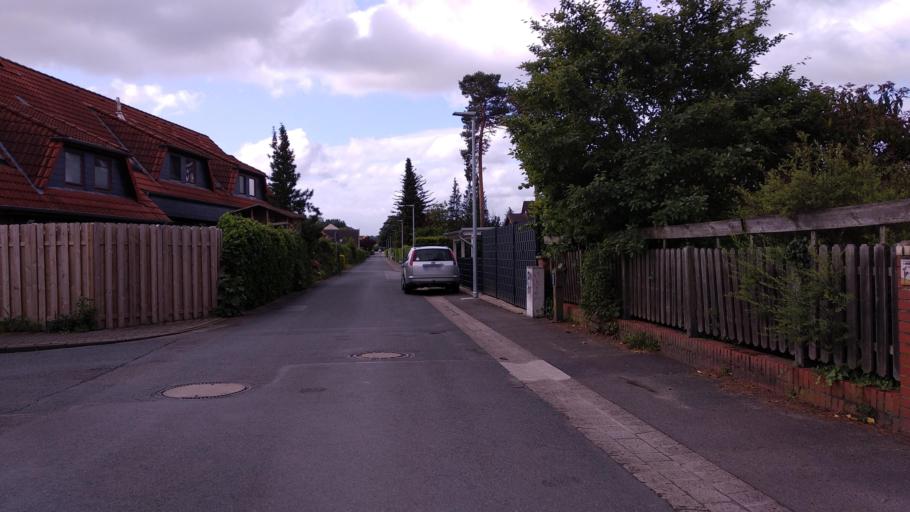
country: DE
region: Lower Saxony
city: Hagenburg
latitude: 52.4590
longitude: 9.3737
